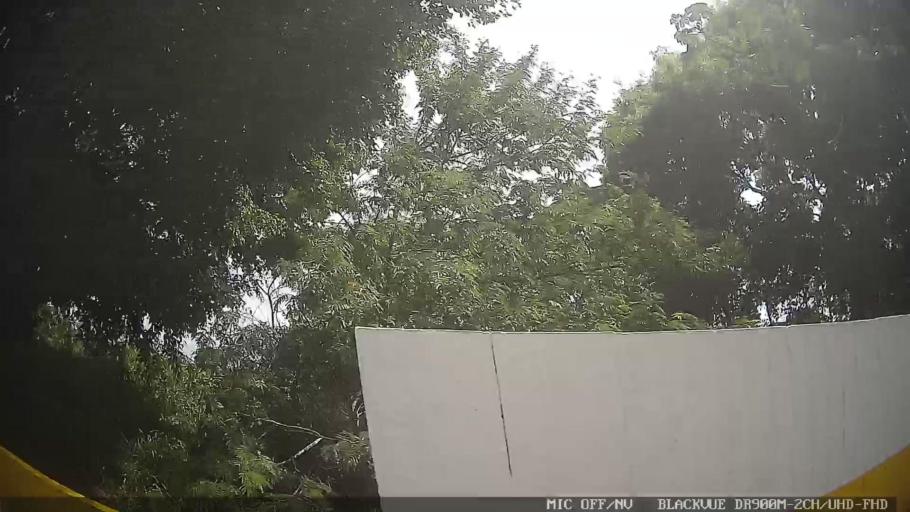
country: BR
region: Sao Paulo
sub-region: Mogi das Cruzes
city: Mogi das Cruzes
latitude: -23.4657
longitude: -46.2586
